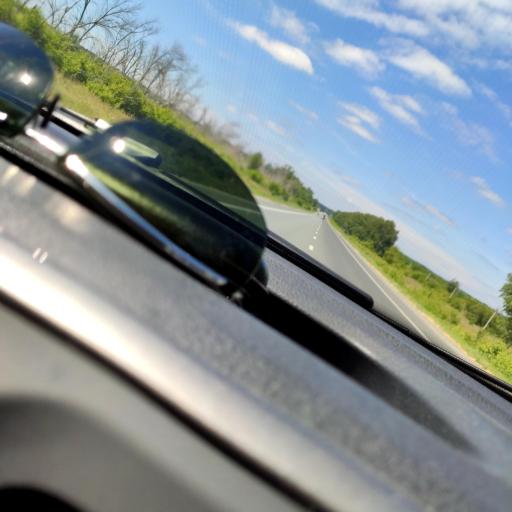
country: RU
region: Samara
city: Kurumoch
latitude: 53.4870
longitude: 50.0075
